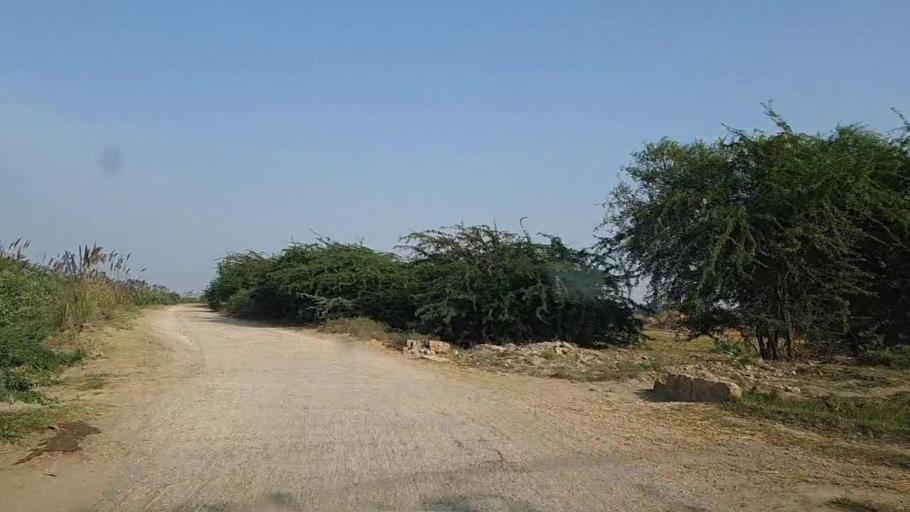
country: PK
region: Sindh
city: Mirpur Sakro
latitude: 24.5951
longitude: 67.5998
